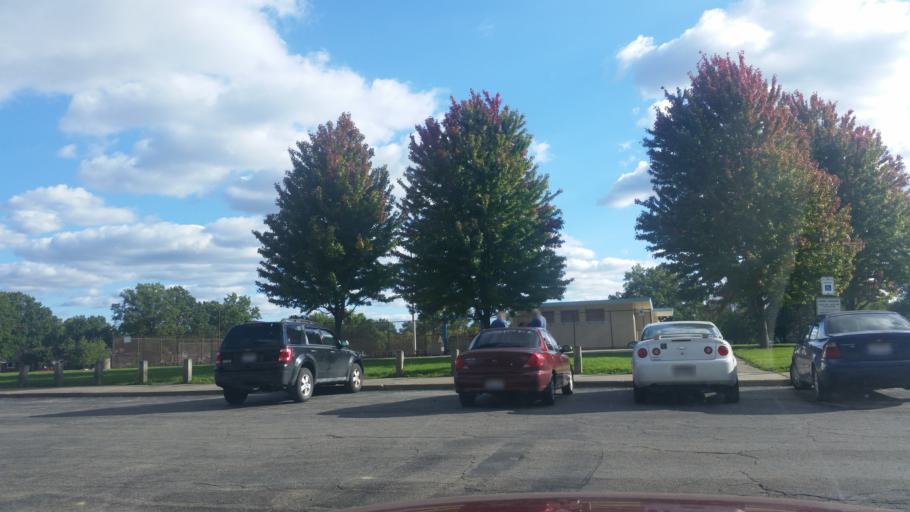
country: US
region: Ohio
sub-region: Cuyahoga County
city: Lakewood
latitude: 41.4666
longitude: -81.8046
